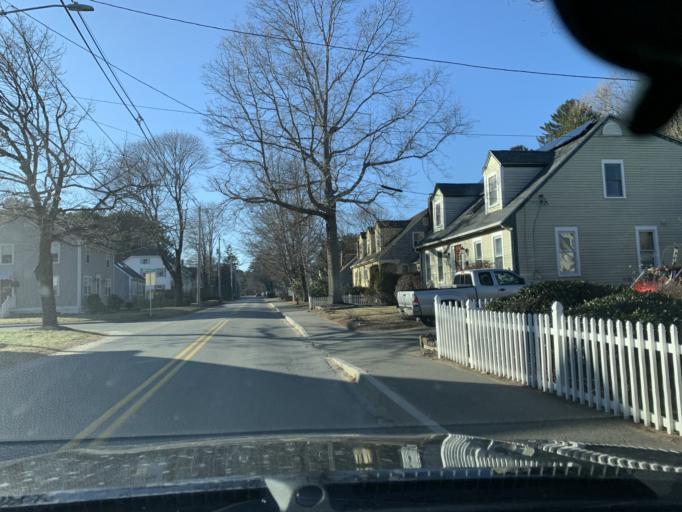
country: US
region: Massachusetts
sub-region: Essex County
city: Essex
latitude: 42.5836
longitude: -70.7754
